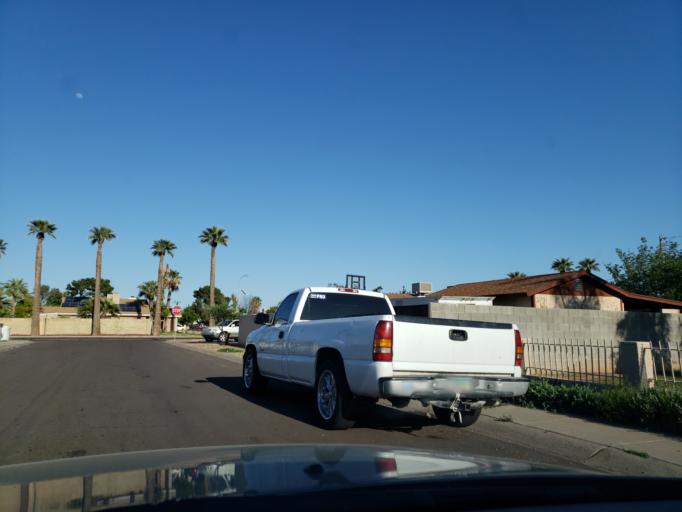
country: US
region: Arizona
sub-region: Maricopa County
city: Glendale
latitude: 33.5427
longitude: -112.1608
